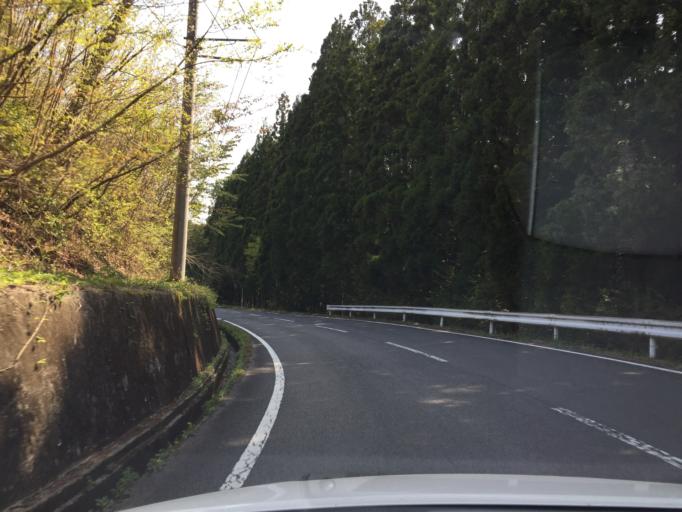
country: JP
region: Fukushima
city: Iwaki
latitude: 37.1641
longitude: 140.8539
